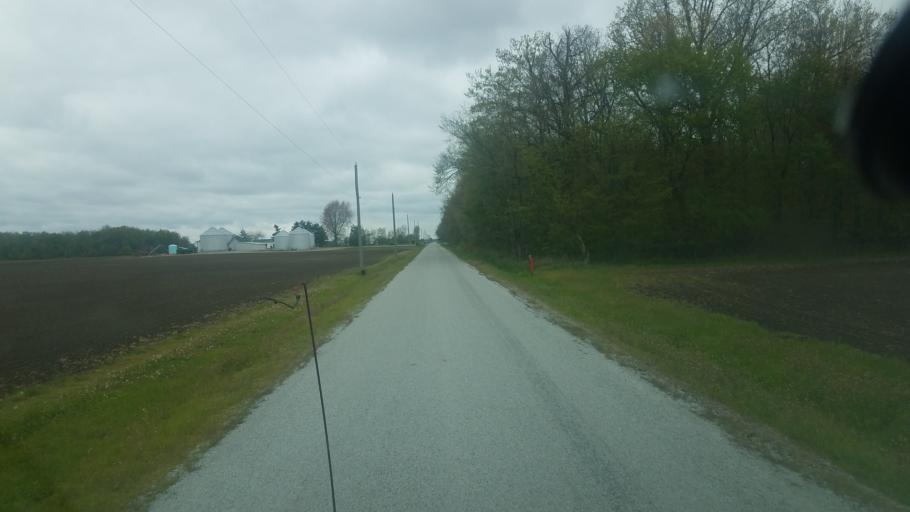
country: US
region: Ohio
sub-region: Hardin County
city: Forest
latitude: 40.7237
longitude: -83.5465
